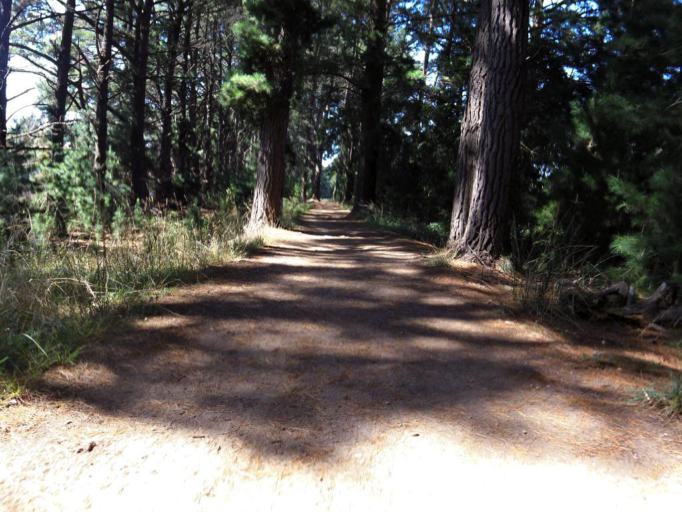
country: AU
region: Victoria
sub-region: Mornington Peninsula
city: Merricks
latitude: -38.3812
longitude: 145.0529
